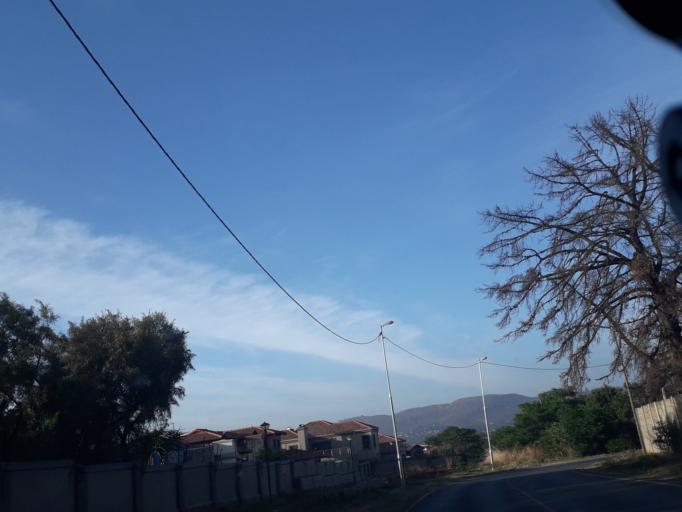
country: ZA
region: Gauteng
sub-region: City of Johannesburg Metropolitan Municipality
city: Roodepoort
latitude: -26.0934
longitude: 27.8997
